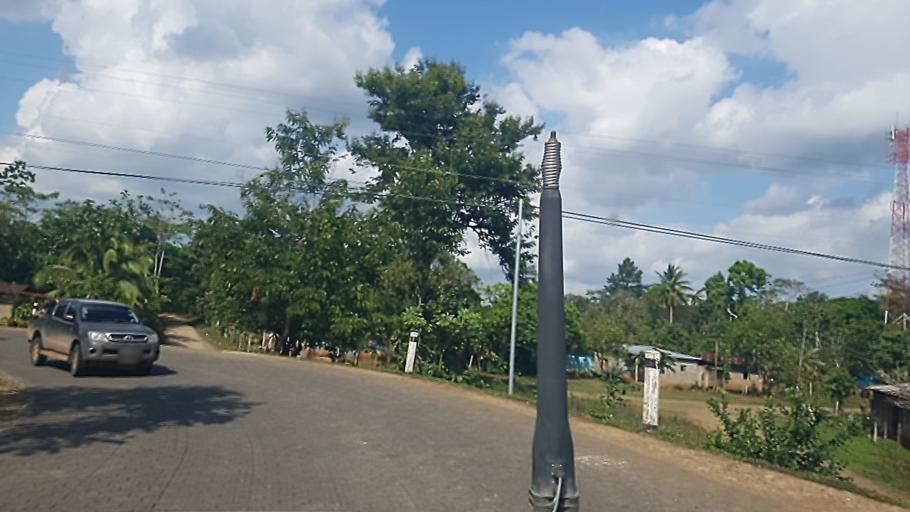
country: NI
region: Atlantico Sur
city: Nueva Guinea
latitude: 11.7015
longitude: -84.3765
